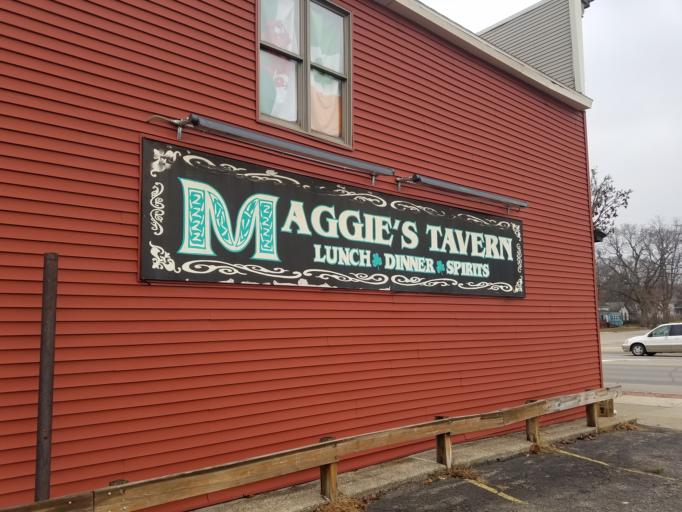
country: US
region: Michigan
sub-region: Wexford County
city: Cadillac
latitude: 44.2545
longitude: -85.4032
